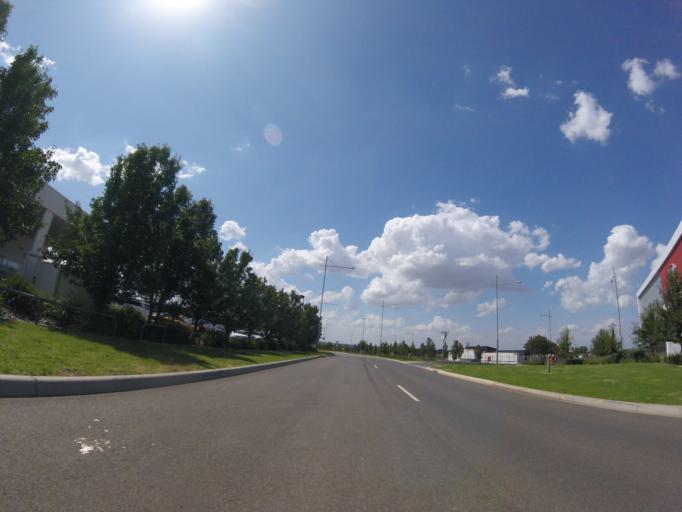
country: AU
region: Victoria
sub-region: Moreland
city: Gowanbrae
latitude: -37.7182
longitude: 144.8958
